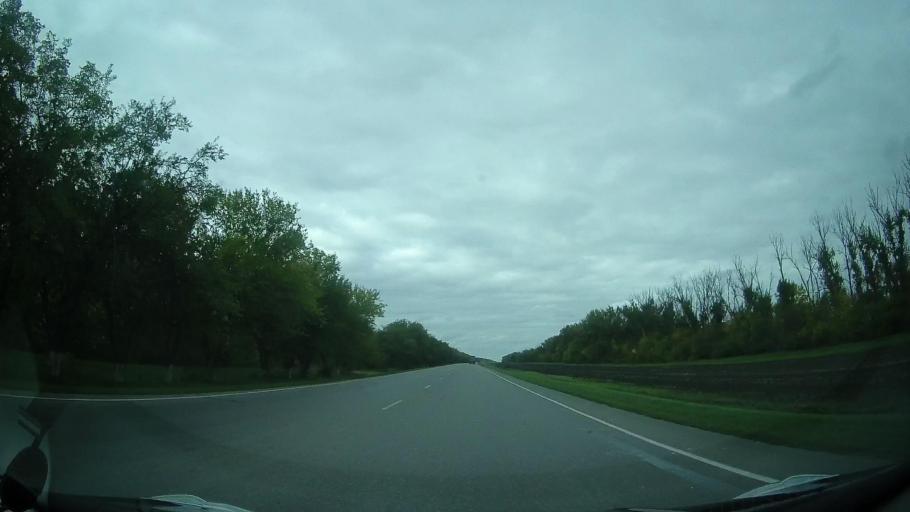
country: RU
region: Rostov
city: Yegorlykskaya
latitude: 46.6140
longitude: 40.6041
